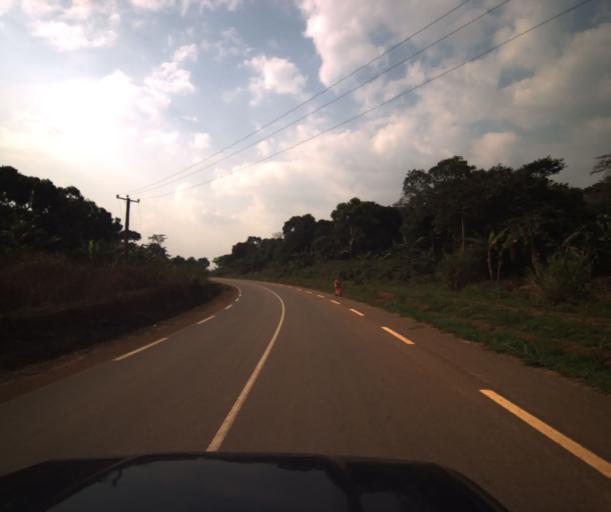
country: CM
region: Centre
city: Mbankomo
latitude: 3.7279
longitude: 11.3918
